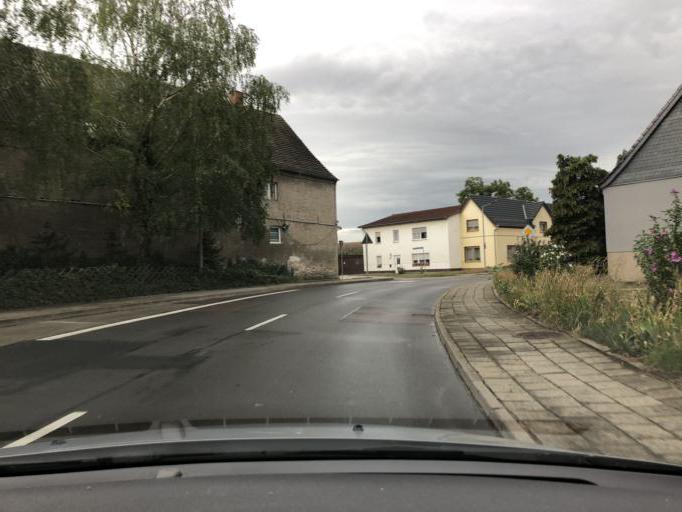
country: DE
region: Saxony-Anhalt
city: Calbe
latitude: 51.8893
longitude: 11.7936
